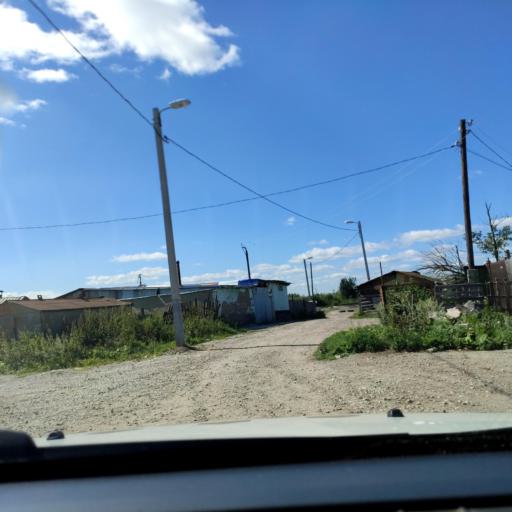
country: RU
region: Perm
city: Kondratovo
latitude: 58.0034
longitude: 56.0916
